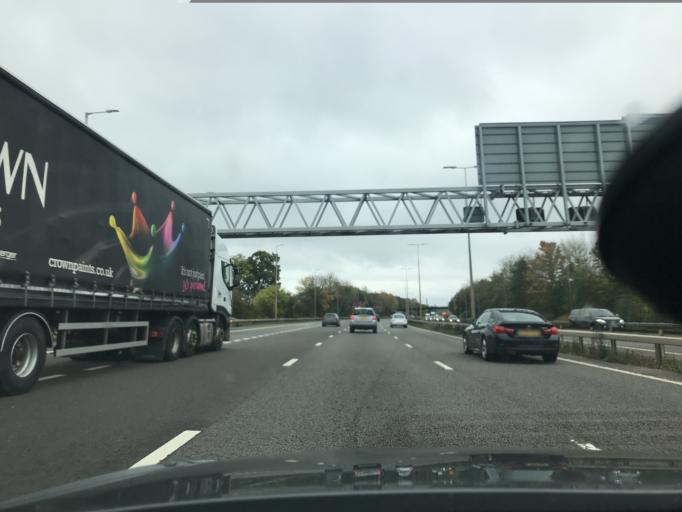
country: GB
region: England
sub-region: Solihull
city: Cheswick Green
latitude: 52.3467
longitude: -1.8004
